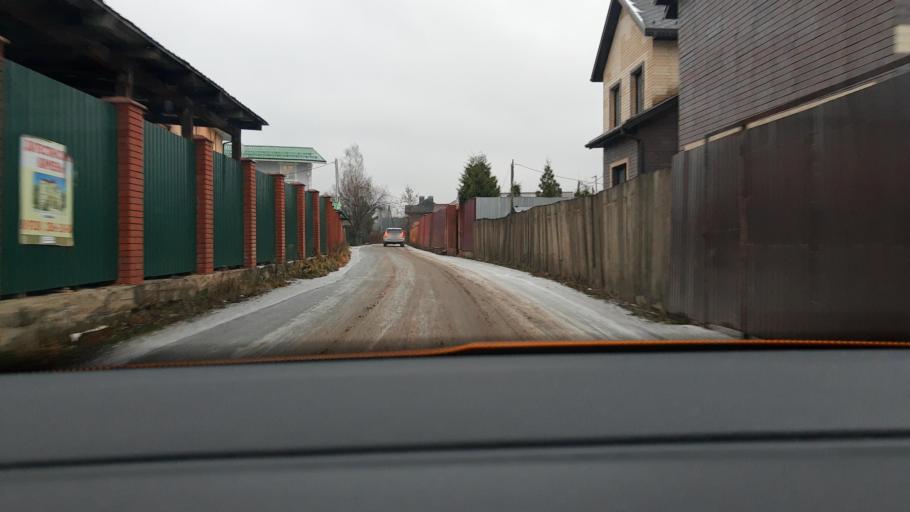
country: RU
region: Moscow
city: Severnyy
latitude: 55.9562
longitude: 37.5584
